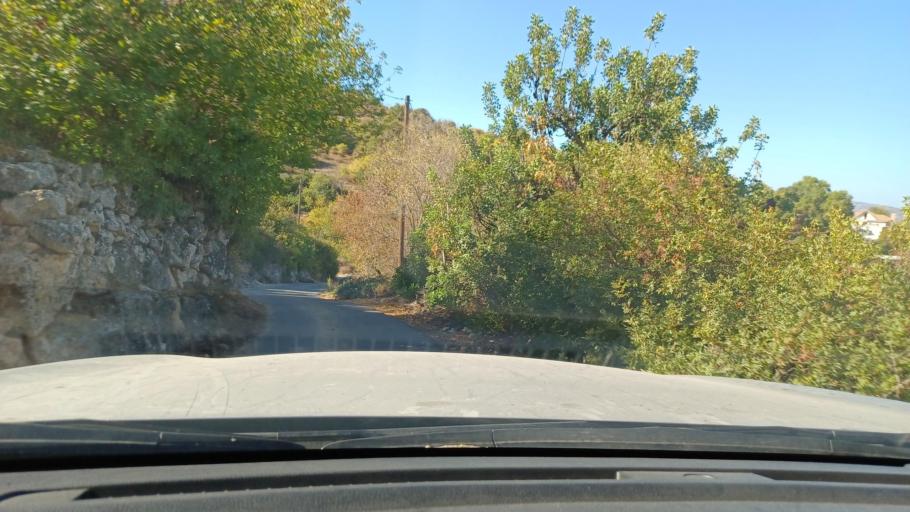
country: CY
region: Pafos
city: Polis
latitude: 34.9949
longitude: 32.5164
